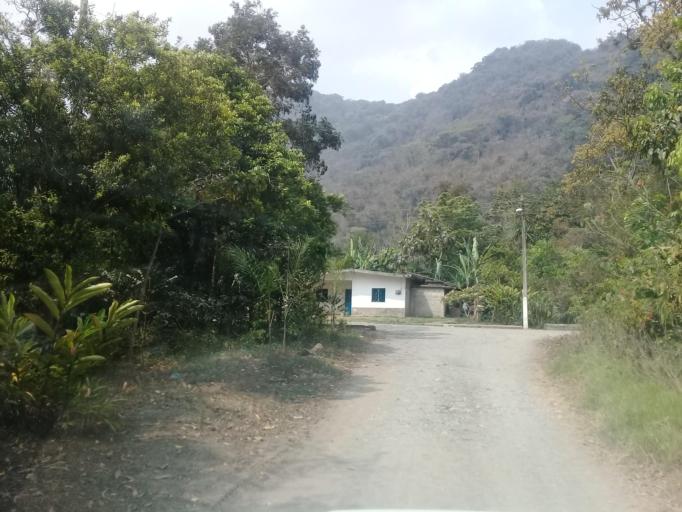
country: MX
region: Veracruz
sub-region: Ixtaczoquitlan
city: Capoluca
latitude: 18.8201
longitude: -96.9927
